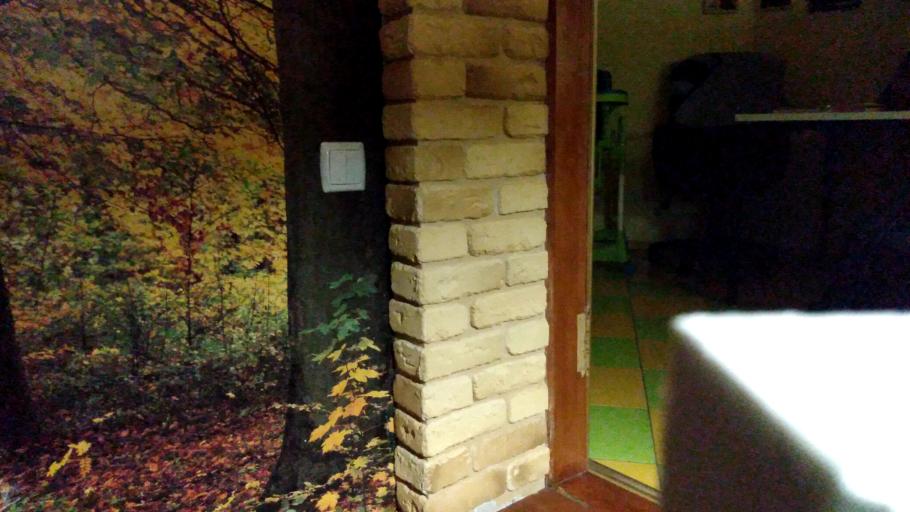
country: RU
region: Vologda
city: Lipin Bor
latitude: 60.9521
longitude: 37.9781
